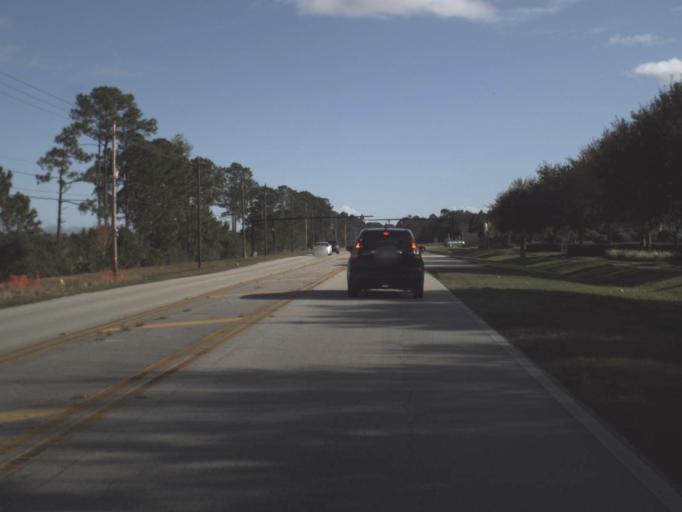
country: US
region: Florida
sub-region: Volusia County
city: Ormond Beach
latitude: 29.2482
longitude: -81.1074
